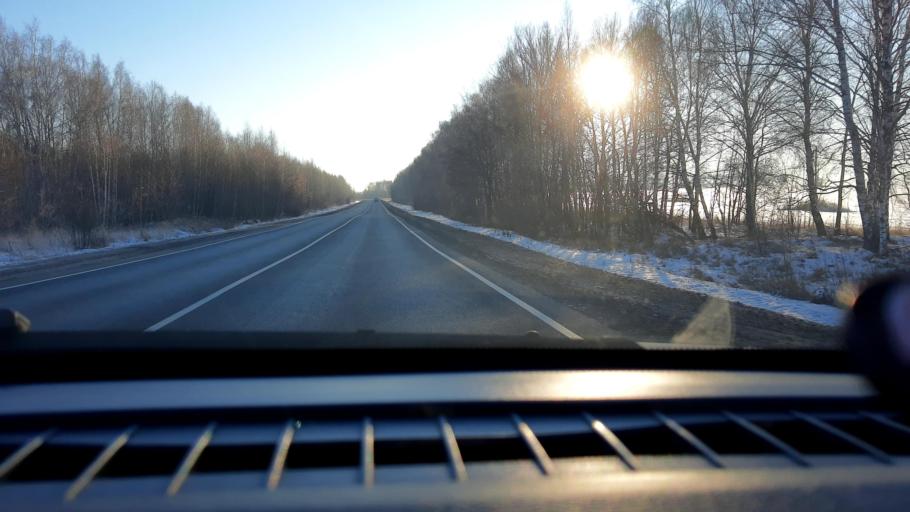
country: RU
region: Nizjnij Novgorod
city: Kstovo
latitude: 56.0602
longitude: 44.1395
